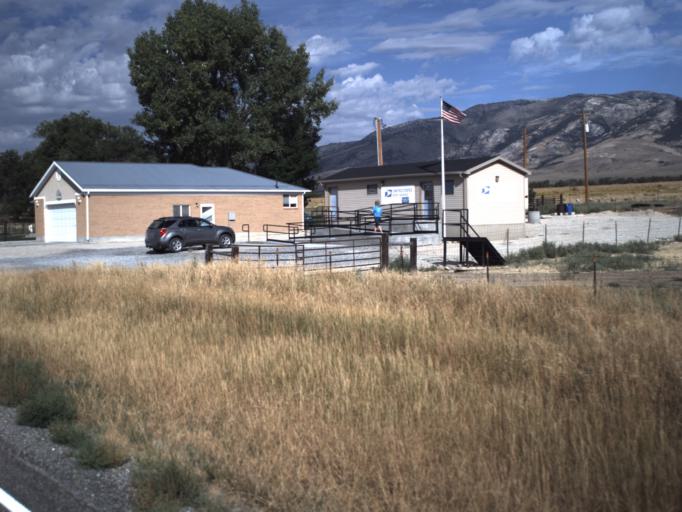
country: US
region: Idaho
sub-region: Cassia County
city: Burley
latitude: 41.8184
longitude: -113.4158
